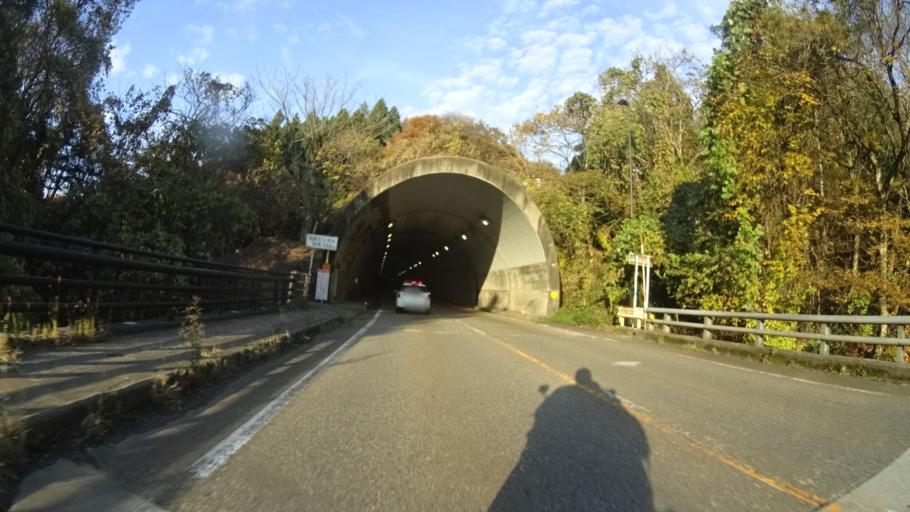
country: JP
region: Niigata
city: Kashiwazaki
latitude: 37.4076
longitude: 138.6603
